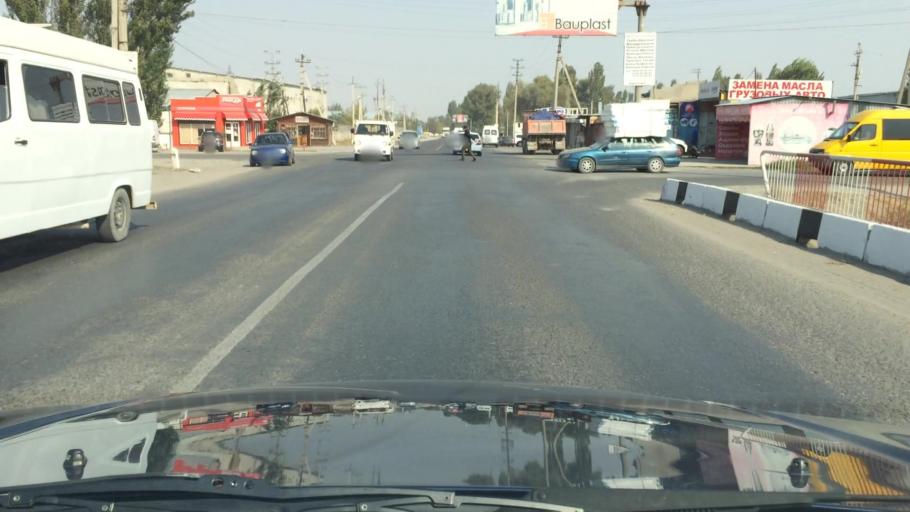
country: KG
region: Chuy
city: Lebedinovka
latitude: 42.8890
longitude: 74.6793
